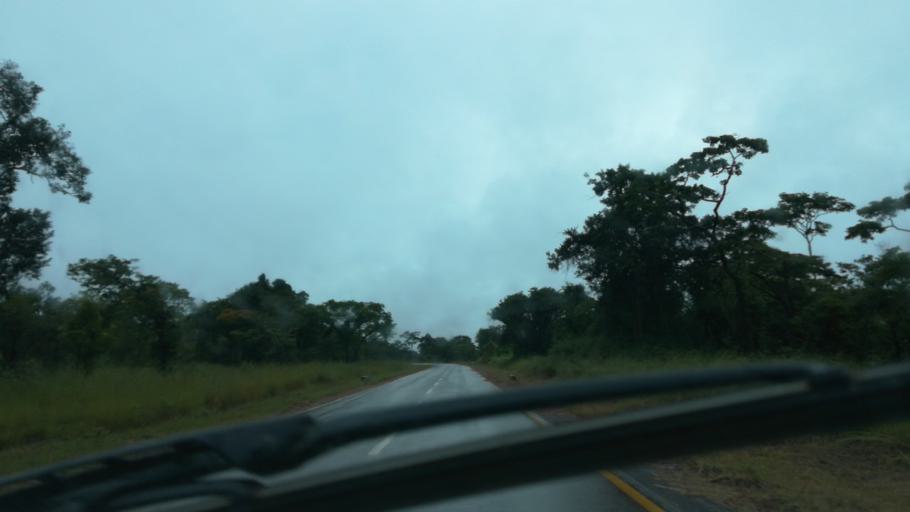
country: ZM
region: Luapula
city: Mwense
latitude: -10.8791
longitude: 28.2195
